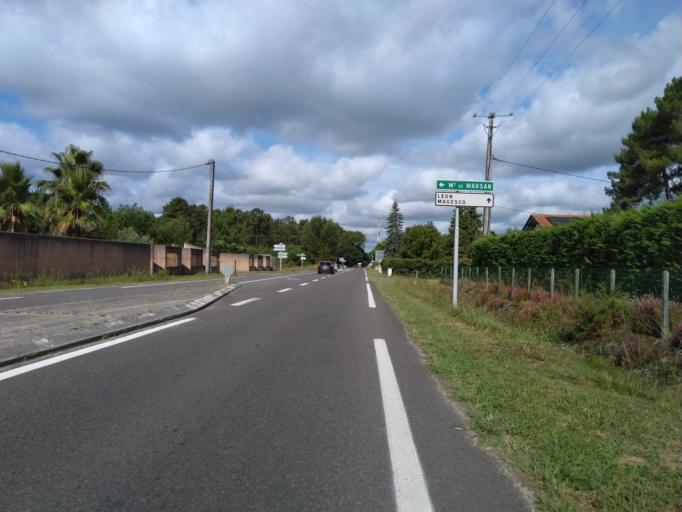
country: FR
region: Aquitaine
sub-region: Departement des Landes
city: Mees
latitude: 43.7320
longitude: -1.1001
